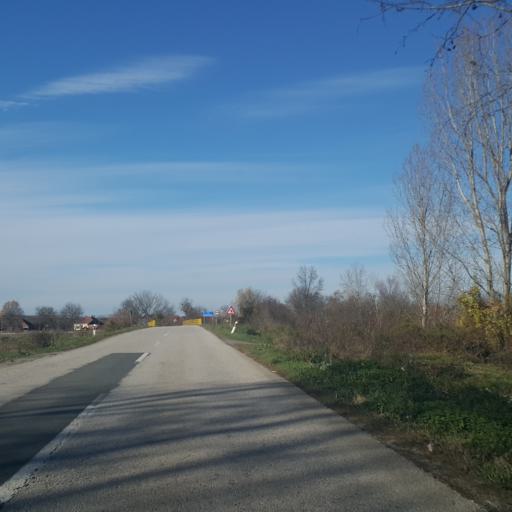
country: RS
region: Central Serbia
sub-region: Sumadijski Okrug
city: Topola
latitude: 44.2570
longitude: 20.8259
